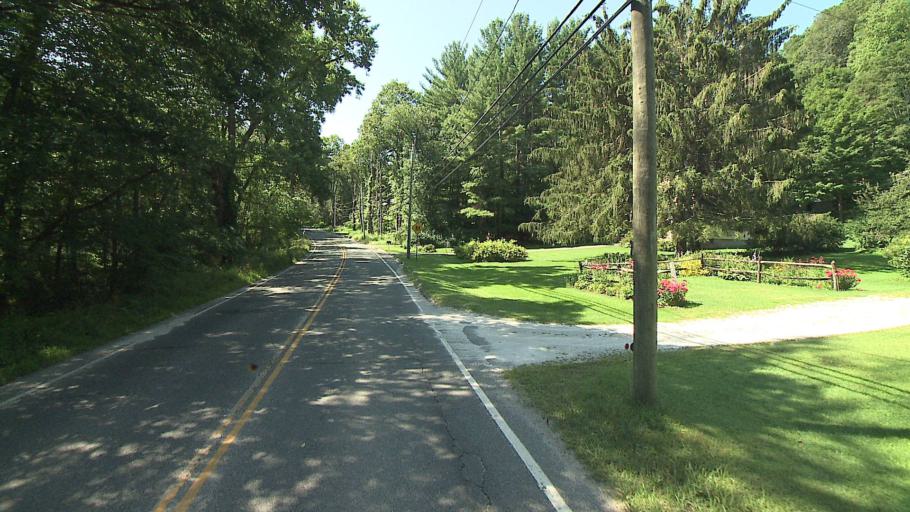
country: US
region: Connecticut
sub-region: Litchfield County
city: Canaan
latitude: 41.9947
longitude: -73.4264
